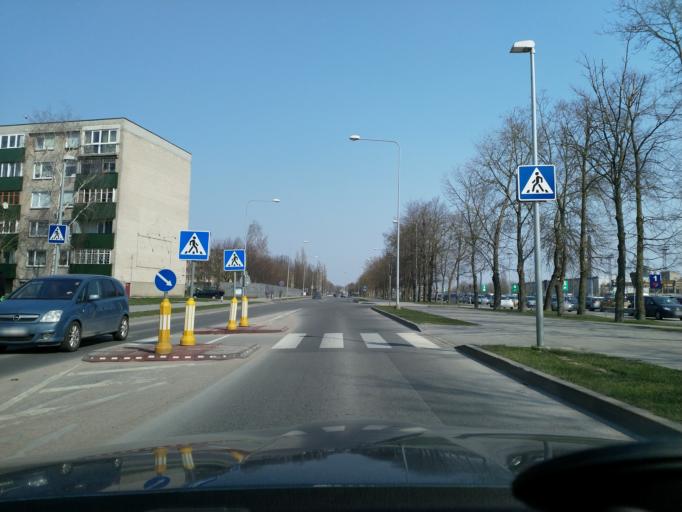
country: LT
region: Klaipedos apskritis
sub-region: Klaipeda
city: Klaipeda
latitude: 55.6947
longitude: 21.1547
